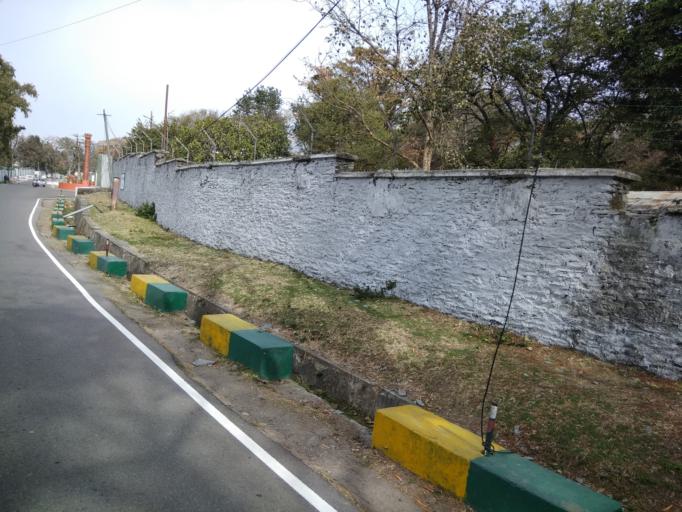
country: IN
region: Himachal Pradesh
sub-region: Kangra
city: Dharmsala
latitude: 32.1753
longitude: 76.3823
